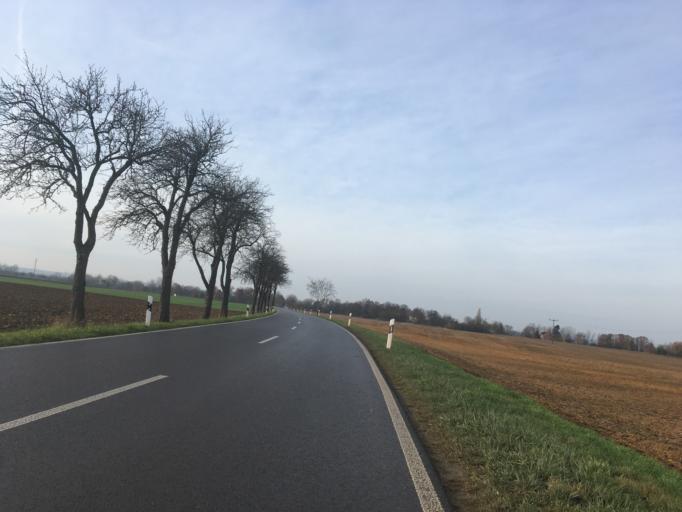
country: DE
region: Brandenburg
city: Wriezen
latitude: 52.7650
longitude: 14.1919
